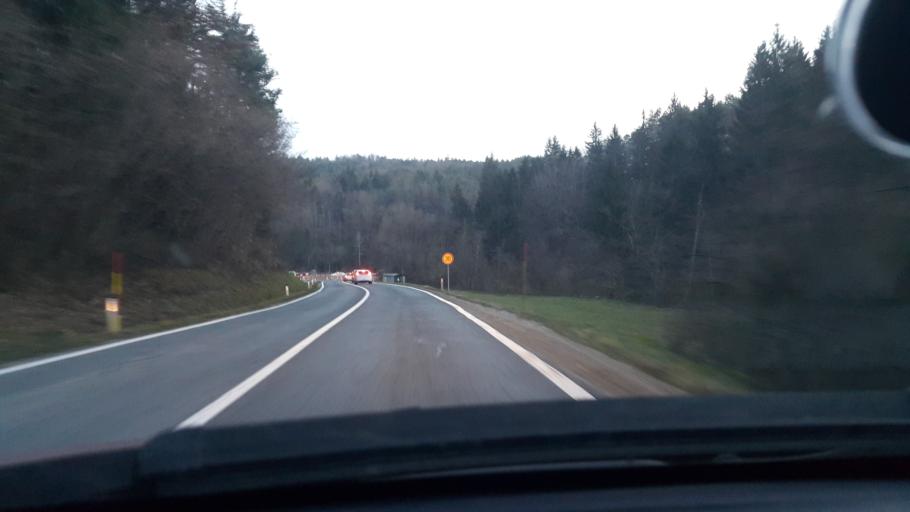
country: SI
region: Dobrna
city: Dobrna
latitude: 46.3349
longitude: 15.1744
